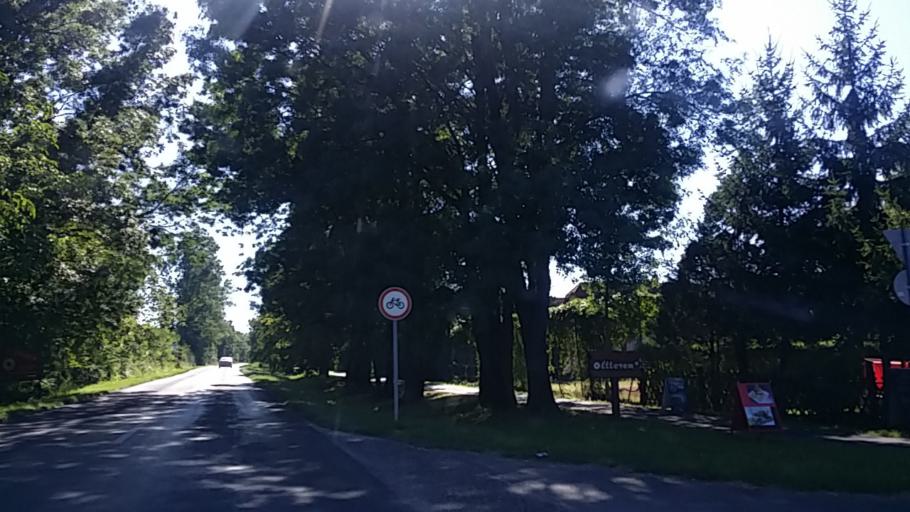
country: HU
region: Somogy
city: Balatonbereny
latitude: 46.7121
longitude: 17.3109
